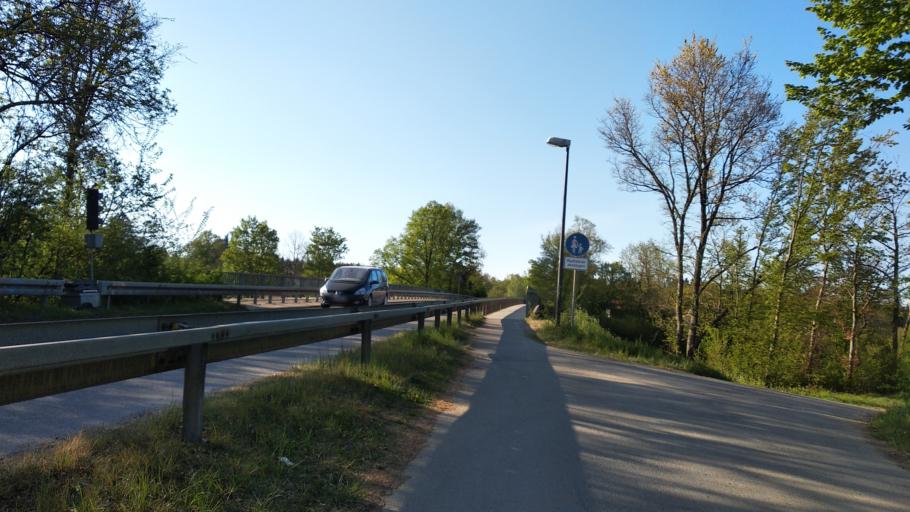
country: DE
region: Bavaria
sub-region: Upper Bavaria
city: Hohenbrunn
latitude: 48.0574
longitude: 11.6990
